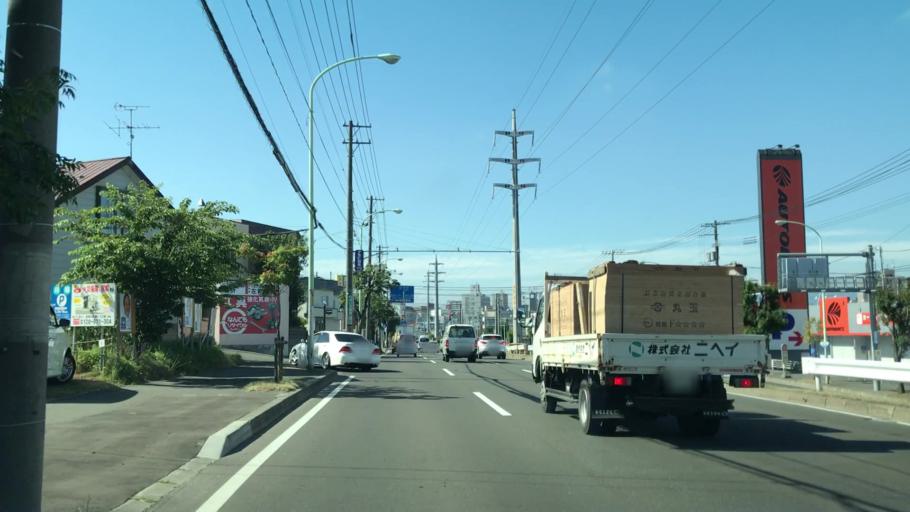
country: JP
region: Hokkaido
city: Sapporo
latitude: 43.0569
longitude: 141.4056
